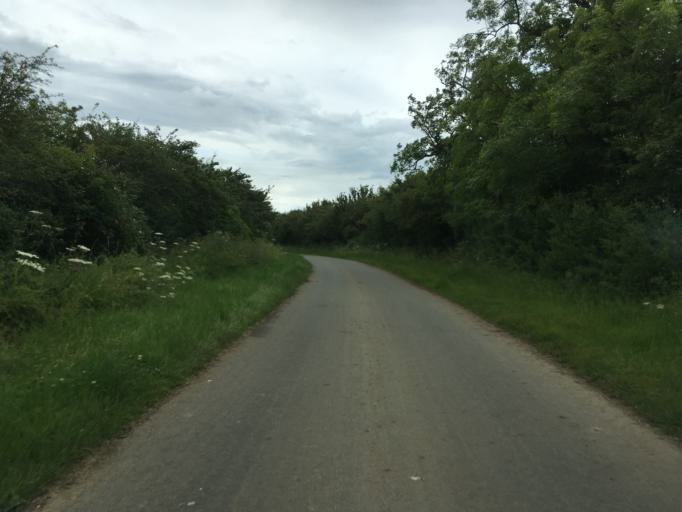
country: GB
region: England
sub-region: Wiltshire
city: Norton
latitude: 51.5970
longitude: -2.1707
